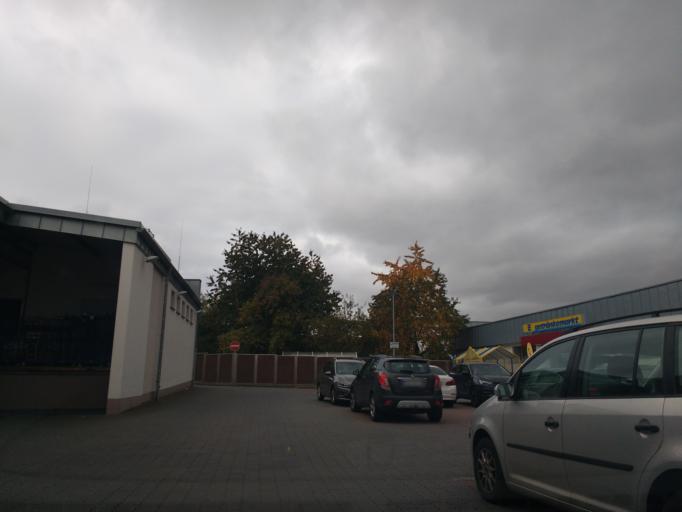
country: DE
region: Thuringia
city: Breitenworbis
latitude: 51.4109
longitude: 10.4248
